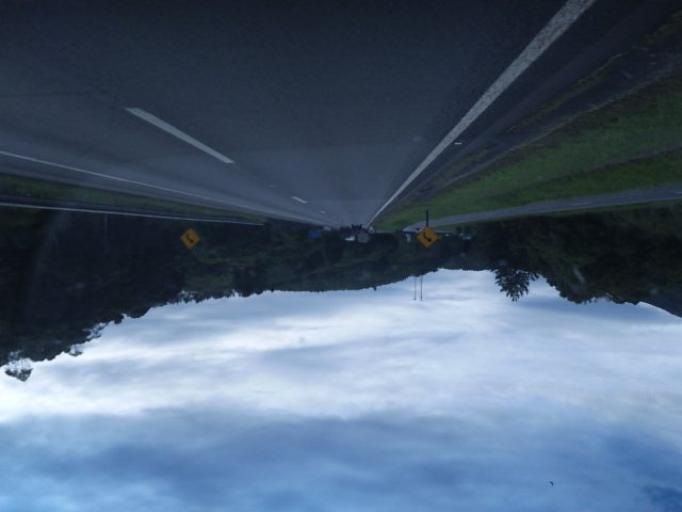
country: BR
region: Parana
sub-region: Campina Grande Do Sul
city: Campina Grande do Sul
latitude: -25.1248
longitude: -48.8567
